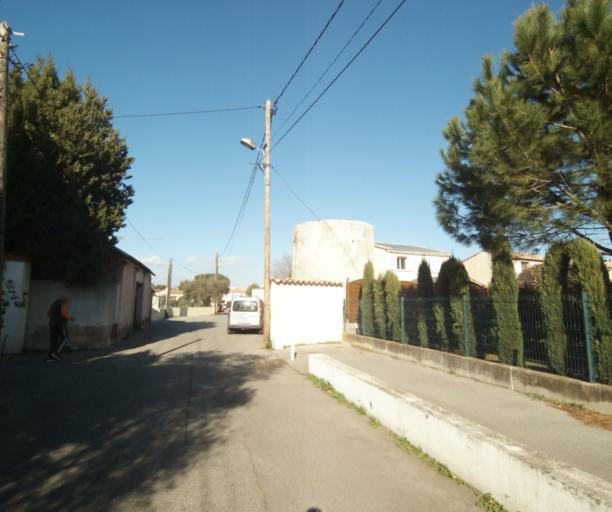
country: FR
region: Provence-Alpes-Cote d'Azur
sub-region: Departement des Alpes-Maritimes
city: Biot
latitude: 43.6076
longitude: 7.1159
